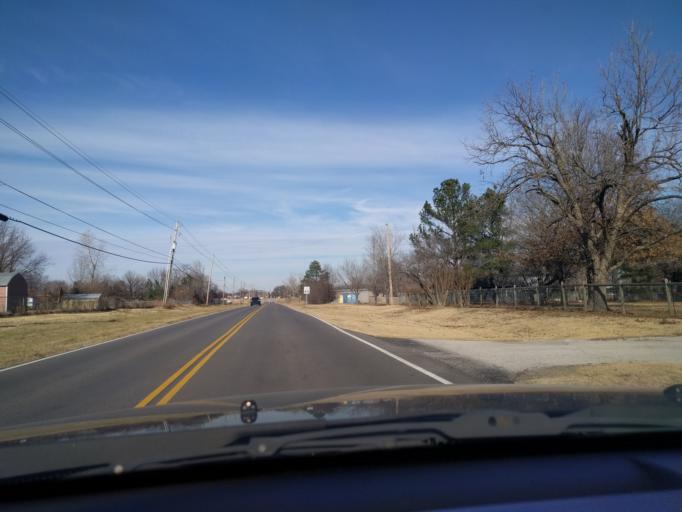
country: US
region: Oklahoma
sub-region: Tulsa County
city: Broken Arrow
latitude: 36.0567
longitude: -95.7081
